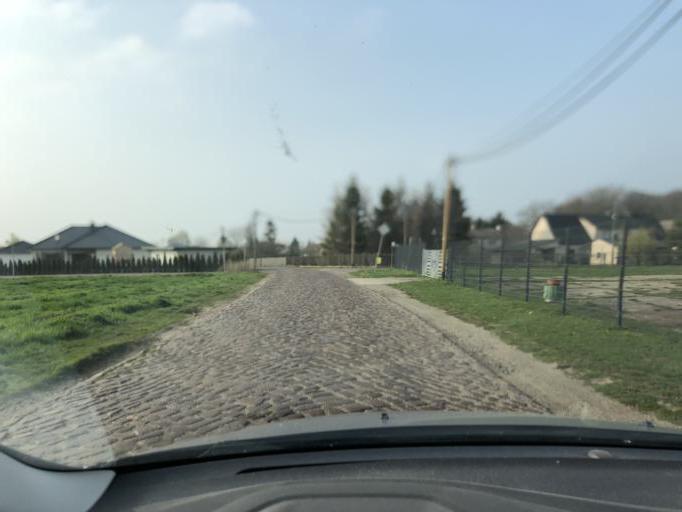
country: DE
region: Saxony-Anhalt
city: Zorbig
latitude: 51.6004
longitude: 12.1147
